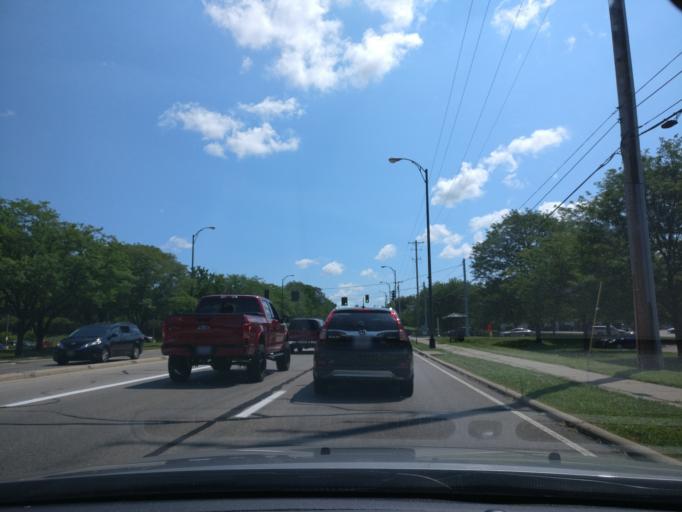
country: US
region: Ohio
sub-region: Montgomery County
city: Centerville
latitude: 39.6279
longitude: -84.1712
